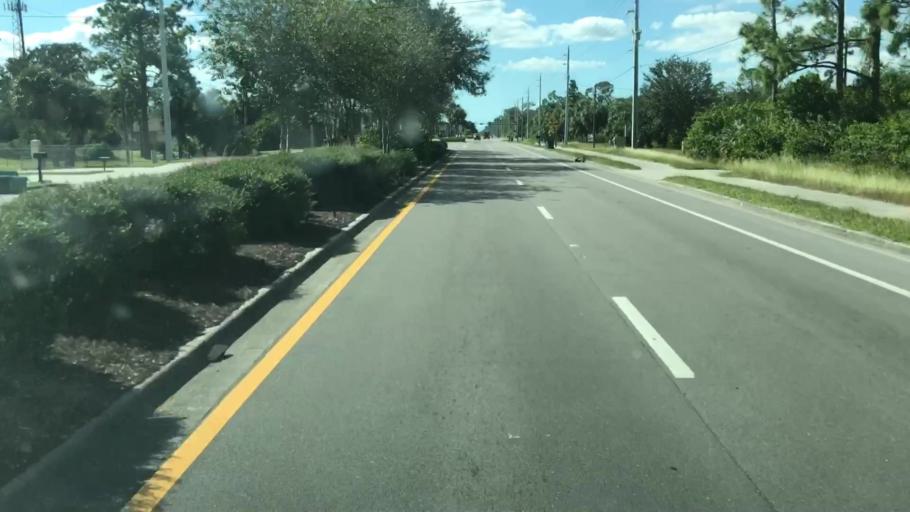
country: US
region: Florida
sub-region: Collier County
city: Orangetree
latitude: 26.2296
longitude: -81.6298
